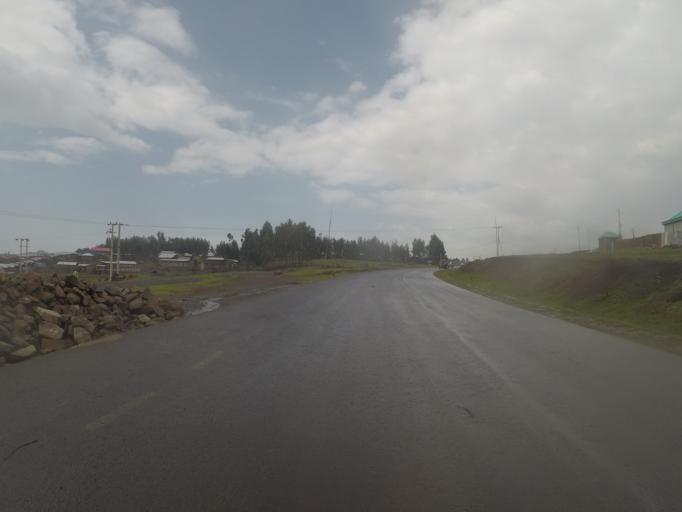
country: ET
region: Amhara
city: Debark'
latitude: 13.1362
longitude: 37.8923
